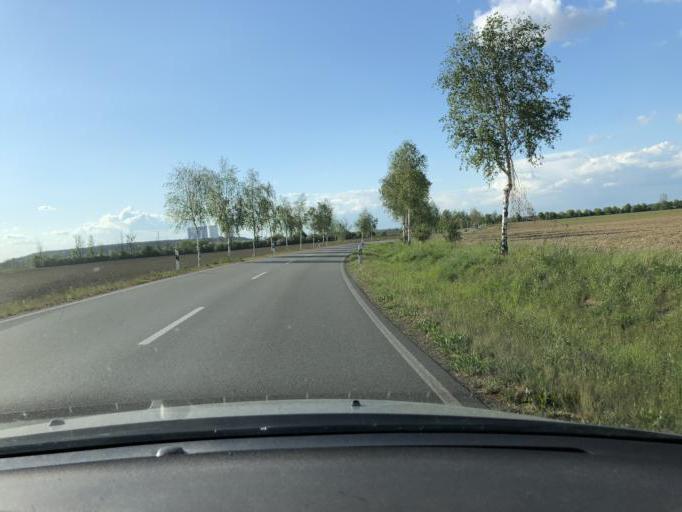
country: DE
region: Saxony
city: Neukieritzsch
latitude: 51.1547
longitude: 12.4234
